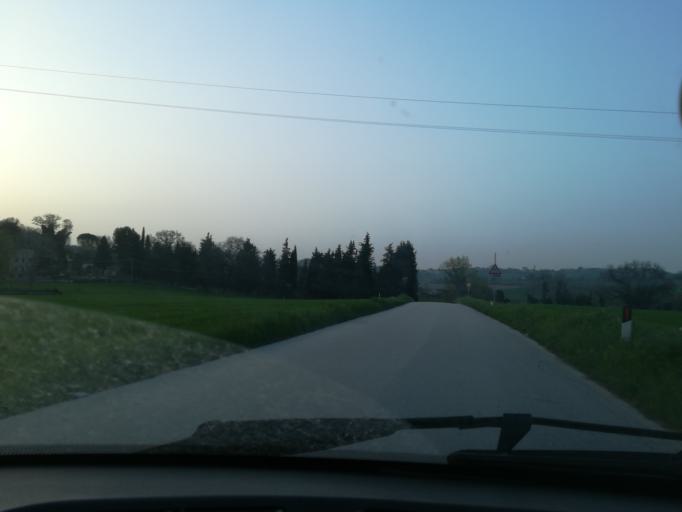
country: IT
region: The Marches
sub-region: Provincia di Macerata
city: Piediripa
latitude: 43.2686
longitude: 13.4624
